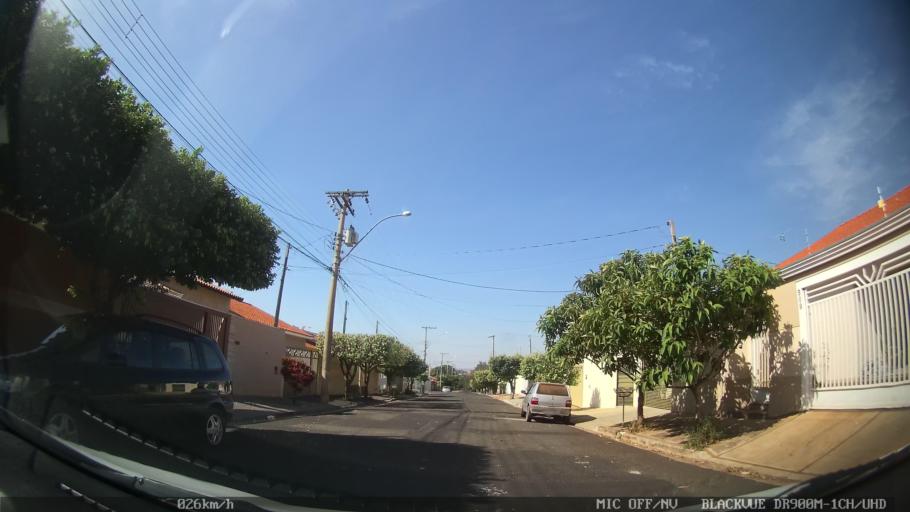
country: BR
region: Sao Paulo
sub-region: Sao Jose Do Rio Preto
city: Sao Jose do Rio Preto
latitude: -20.7883
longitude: -49.4388
